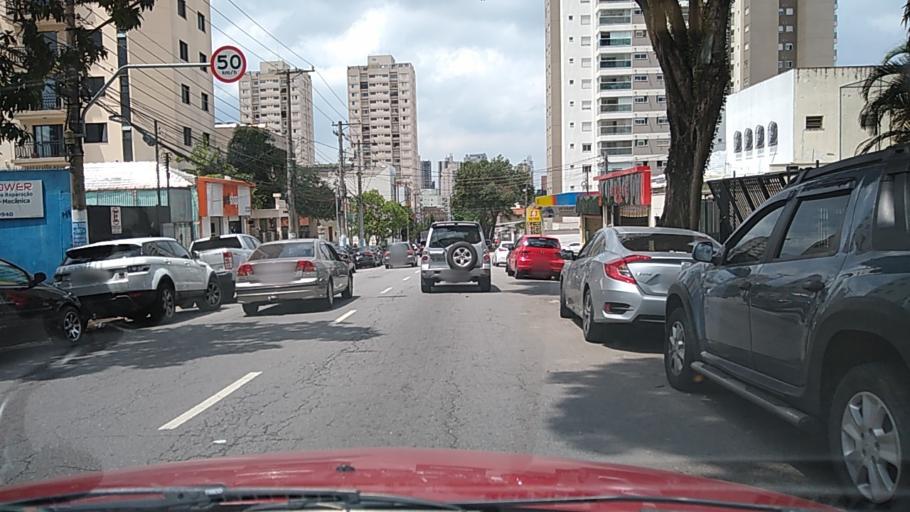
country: BR
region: Sao Paulo
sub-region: Diadema
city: Diadema
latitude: -23.6268
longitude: -46.6345
